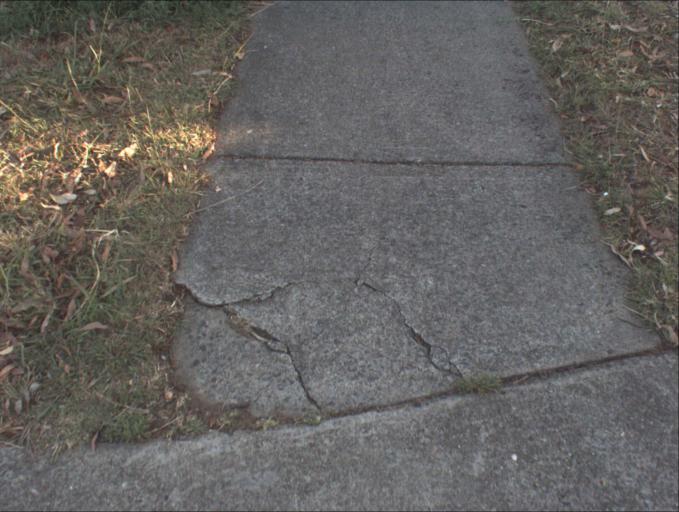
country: AU
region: Queensland
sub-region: Gold Coast
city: Yatala
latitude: -27.7110
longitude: 153.2142
